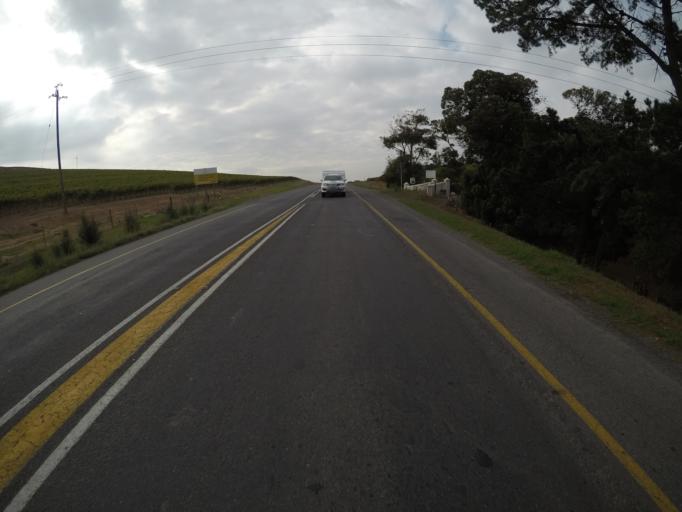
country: ZA
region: Western Cape
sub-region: City of Cape Town
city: Sunset Beach
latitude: -33.8348
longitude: 18.5910
